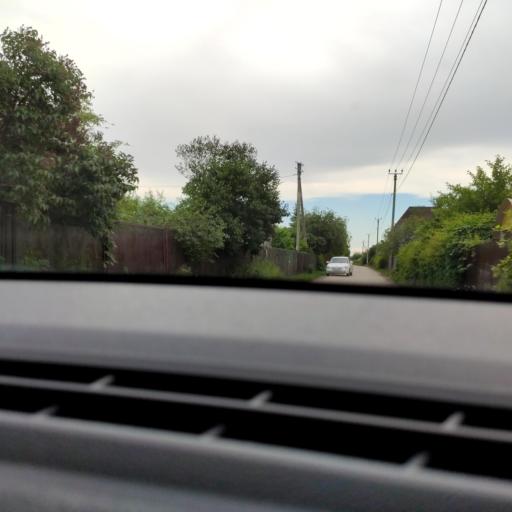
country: RU
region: Samara
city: Podstepki
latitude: 53.5124
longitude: 49.0729
